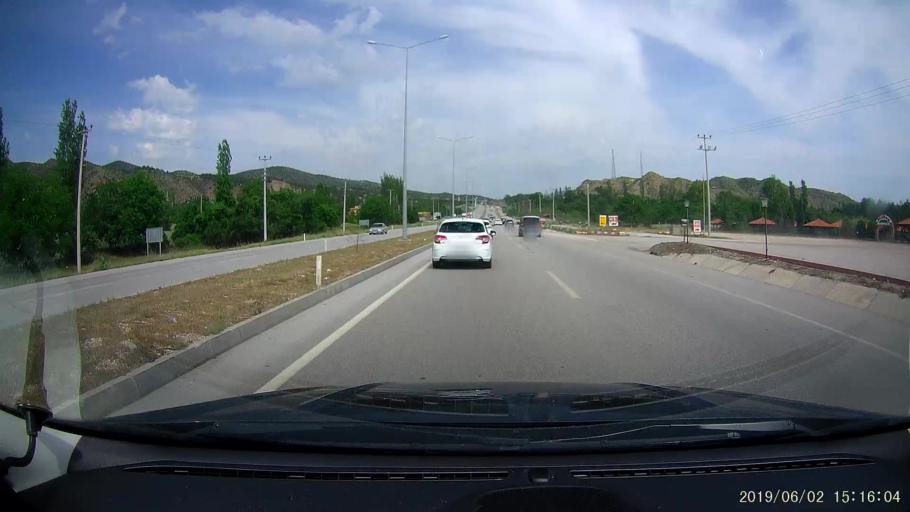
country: TR
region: Corum
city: Osmancik
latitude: 40.9702
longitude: 34.8590
